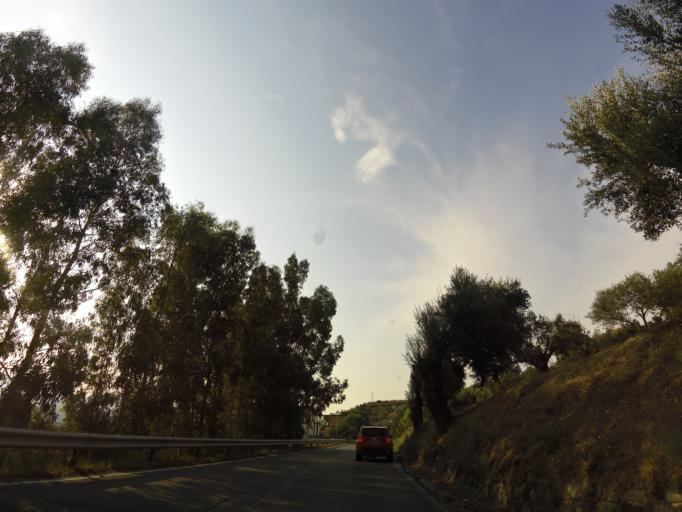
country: IT
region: Calabria
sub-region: Provincia di Reggio Calabria
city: Monasterace
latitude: 38.4510
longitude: 16.5303
